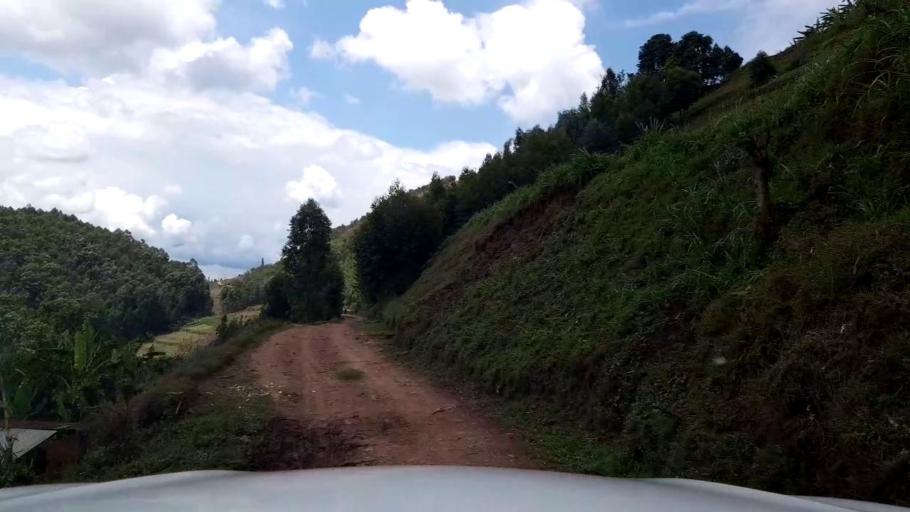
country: RW
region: Northern Province
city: Byumba
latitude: -1.5255
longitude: 30.1309
